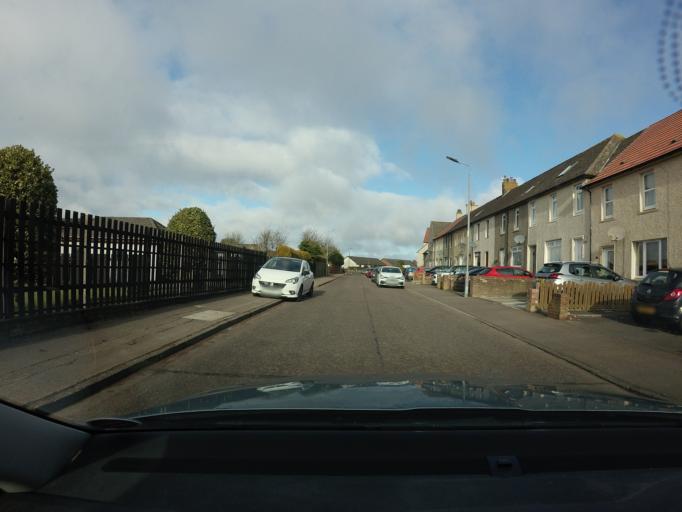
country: GB
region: Scotland
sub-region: South Lanarkshire
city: Forth
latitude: 55.7628
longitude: -3.6958
